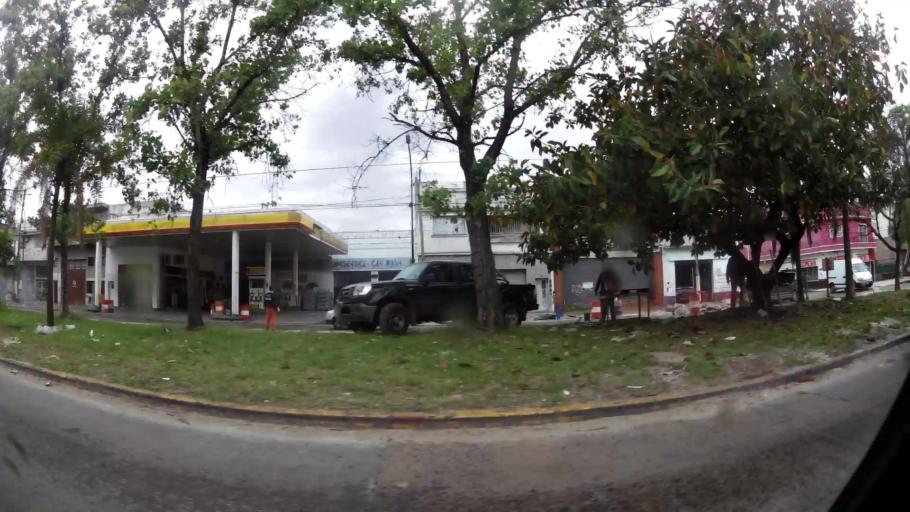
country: AR
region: Buenos Aires
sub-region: Partido de Lanus
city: Lanus
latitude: -34.6786
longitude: -58.4055
